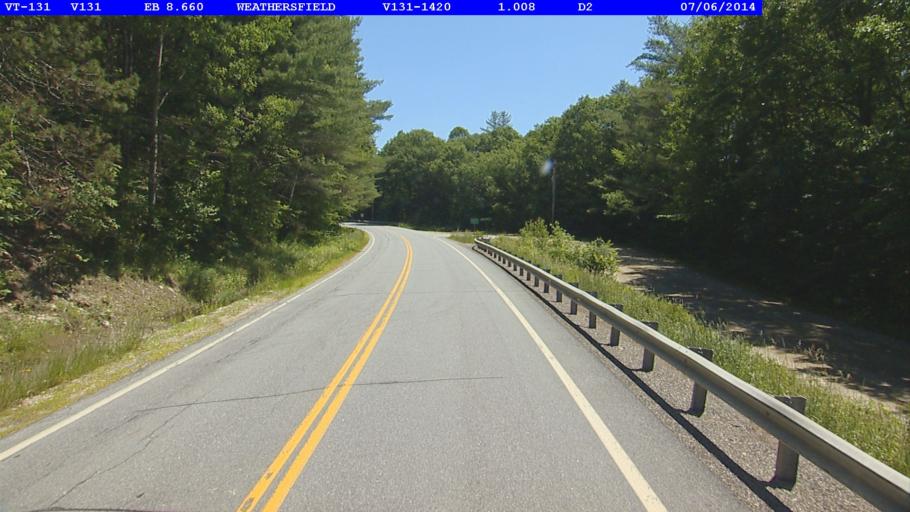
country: US
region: Vermont
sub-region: Windsor County
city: Springfield
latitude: 43.3989
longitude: -72.5216
